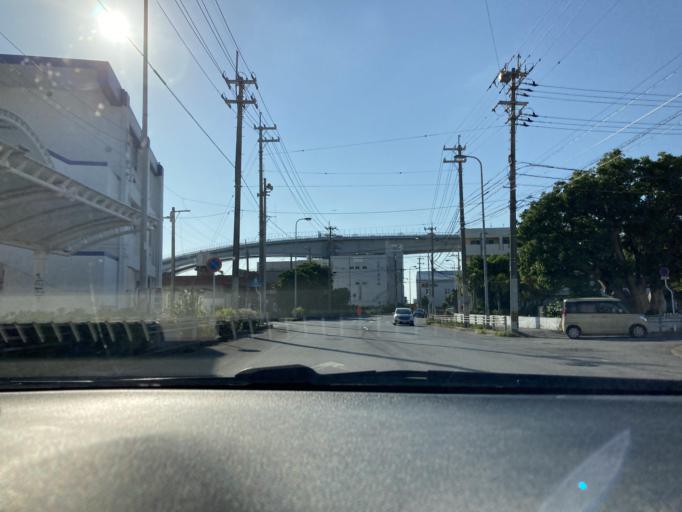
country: JP
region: Okinawa
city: Naha-shi
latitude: 26.2265
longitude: 127.6831
